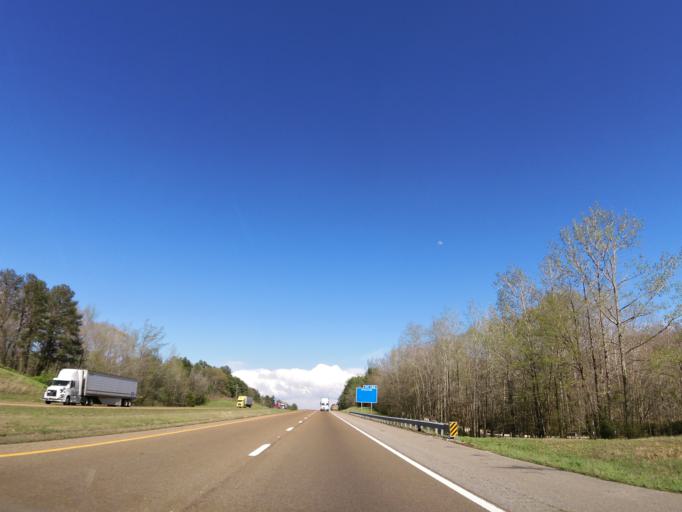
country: US
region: Tennessee
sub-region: Decatur County
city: Parsons
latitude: 35.8245
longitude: -88.1235
